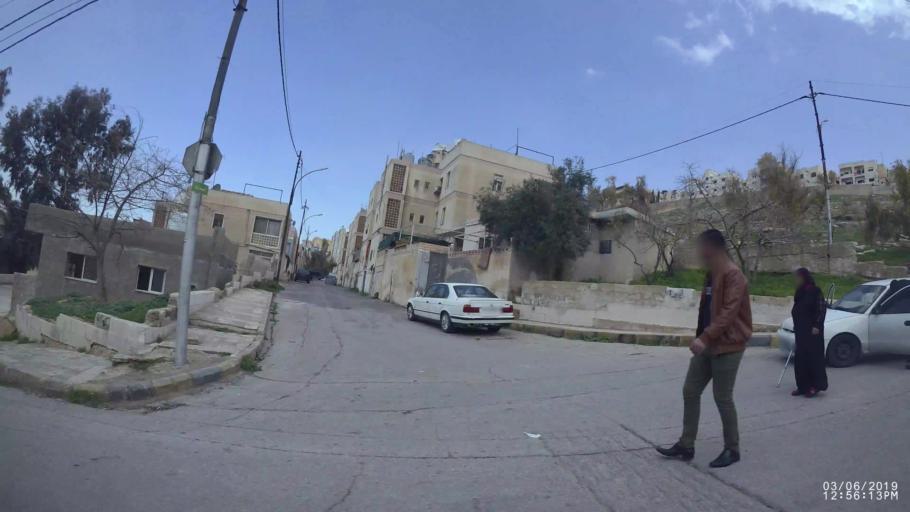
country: JO
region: Amman
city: Amman
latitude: 31.9799
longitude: 35.9783
